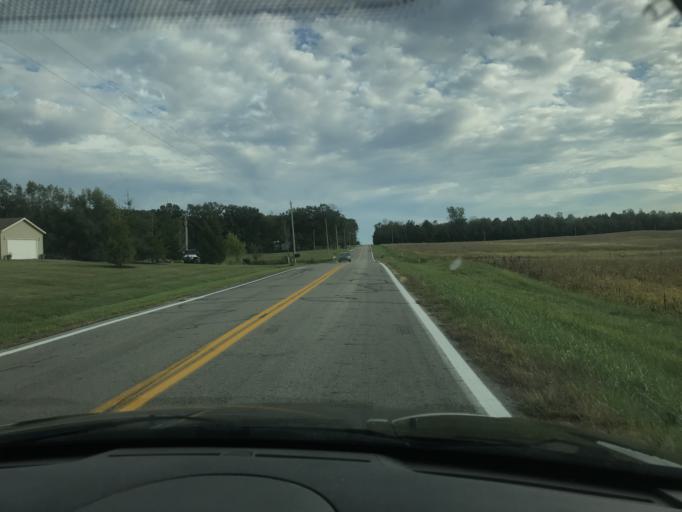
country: US
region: Ohio
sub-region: Champaign County
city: North Lewisburg
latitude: 40.2355
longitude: -83.6448
